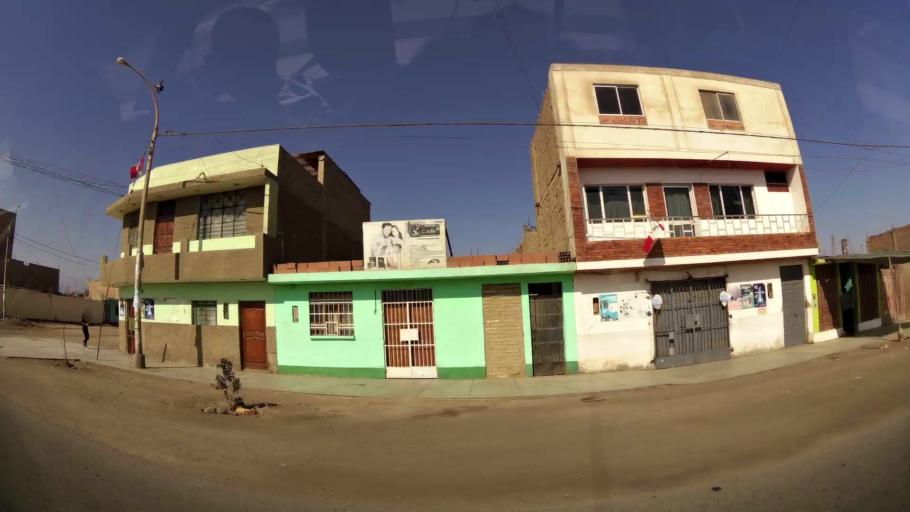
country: PE
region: Ica
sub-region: Provincia de Chincha
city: Chincha Alta
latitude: -13.4082
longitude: -76.1264
